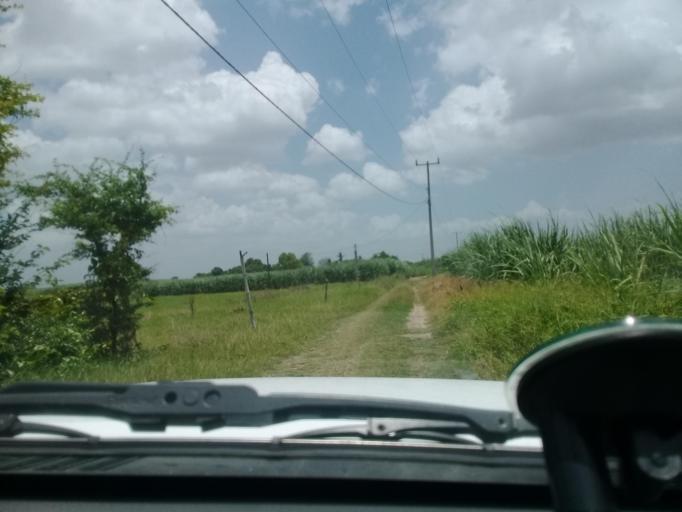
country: MX
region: Veracruz
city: Moralillo
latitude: 22.1325
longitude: -98.0372
